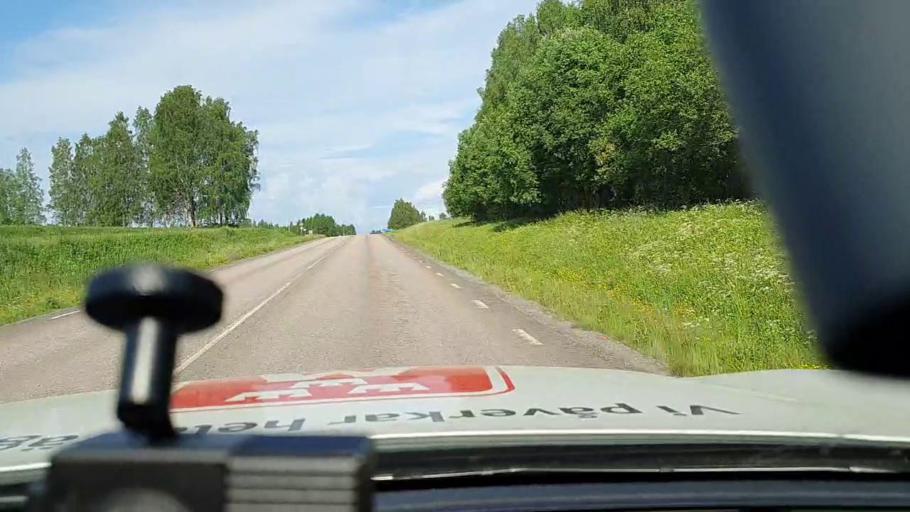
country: SE
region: Norrbotten
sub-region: Alvsbyns Kommun
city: AElvsbyn
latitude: 66.0143
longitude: 21.1649
